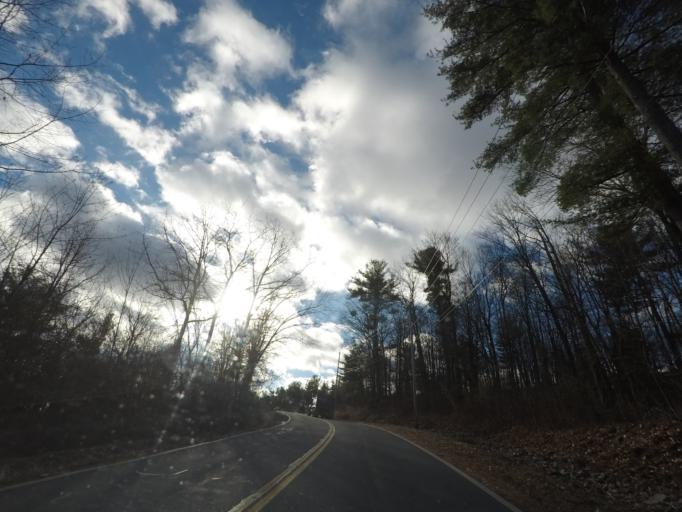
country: US
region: New York
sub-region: Saratoga County
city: Waterford
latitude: 42.8362
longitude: -73.6790
